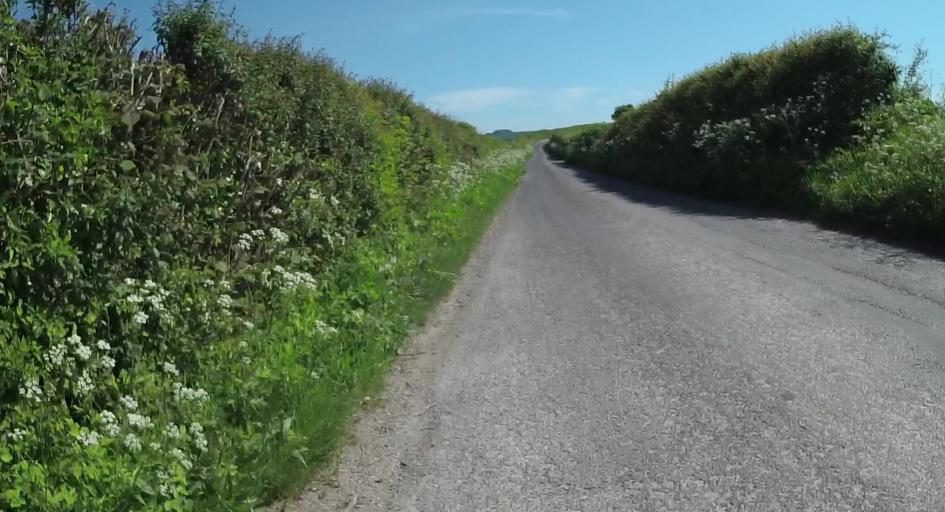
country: GB
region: England
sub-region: Hampshire
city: Kings Worthy
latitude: 51.0791
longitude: -1.2707
